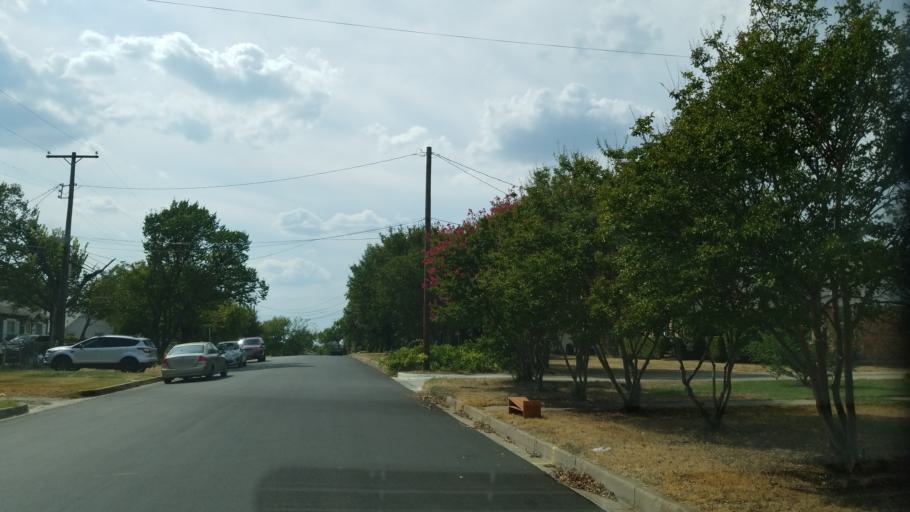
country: US
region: Texas
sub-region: Dallas County
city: Dallas
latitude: 32.7705
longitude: -96.8429
